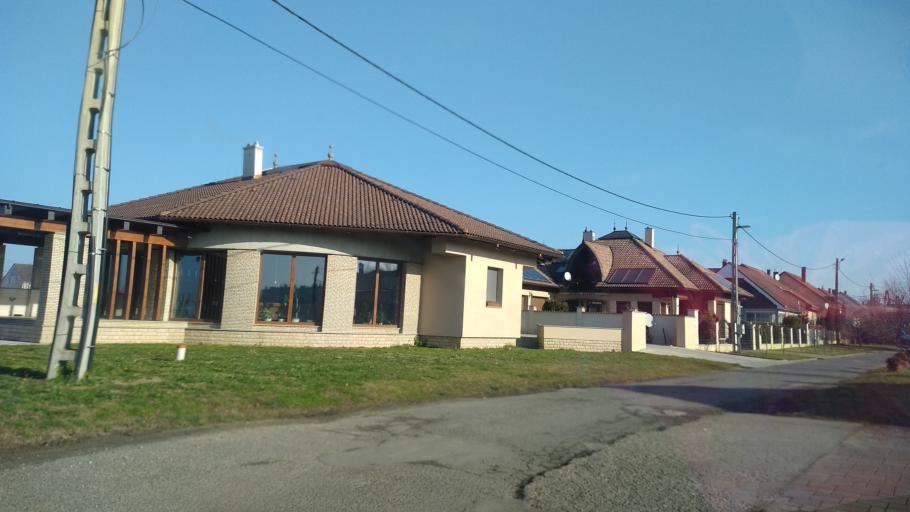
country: HU
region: Somogy
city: Barcs
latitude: 45.9640
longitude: 17.4684
